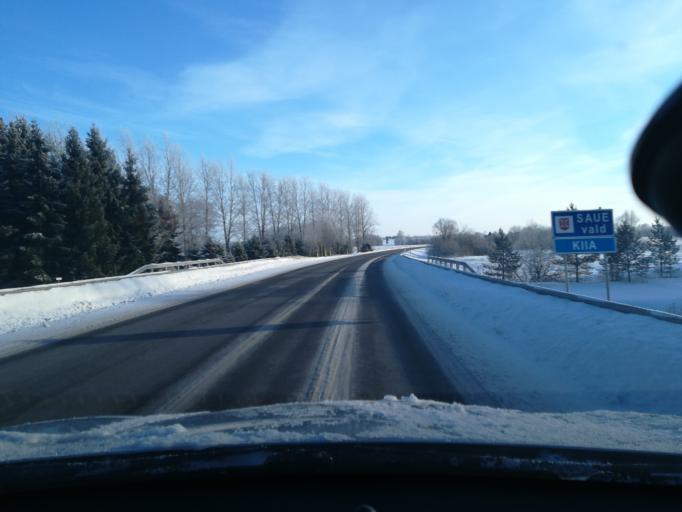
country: EE
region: Harju
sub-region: Harku vald
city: Tabasalu
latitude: 59.3749
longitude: 24.4697
